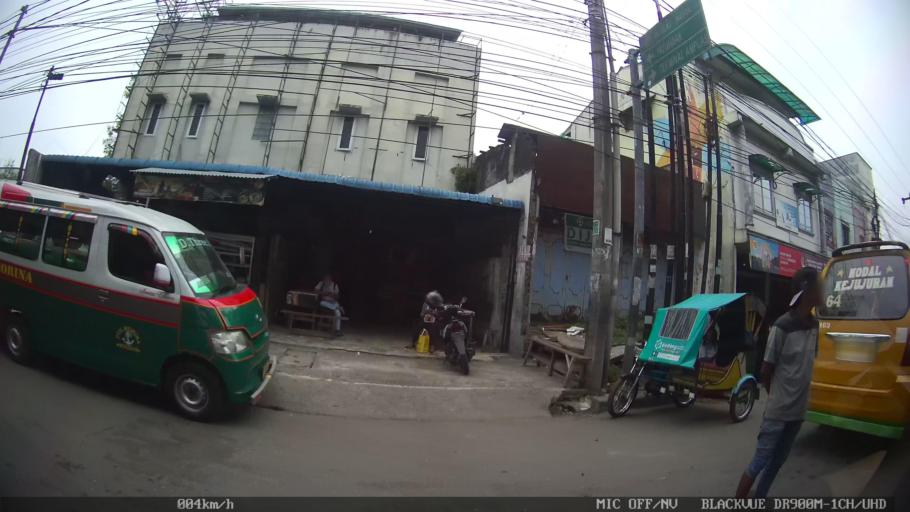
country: ID
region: North Sumatra
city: Deli Tua
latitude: 3.5360
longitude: 98.7188
